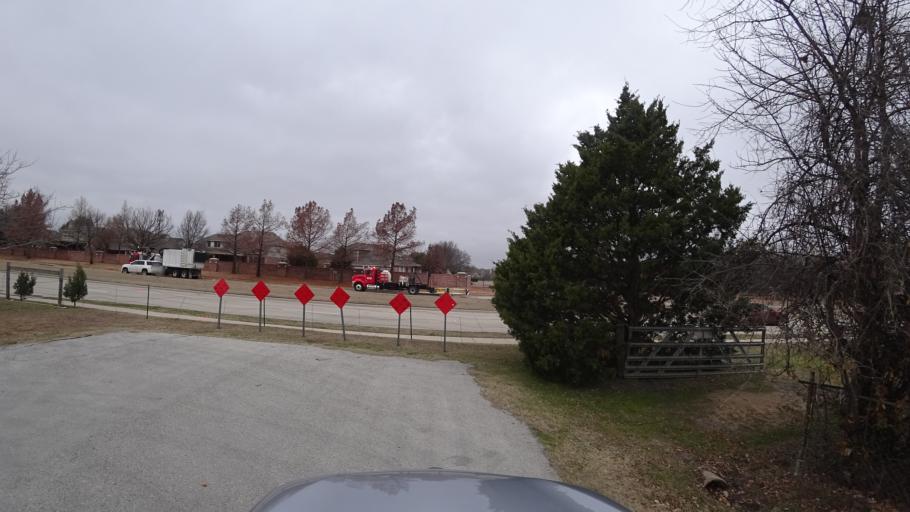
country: US
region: Texas
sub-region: Denton County
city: Lewisville
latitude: 33.0237
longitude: -97.0363
